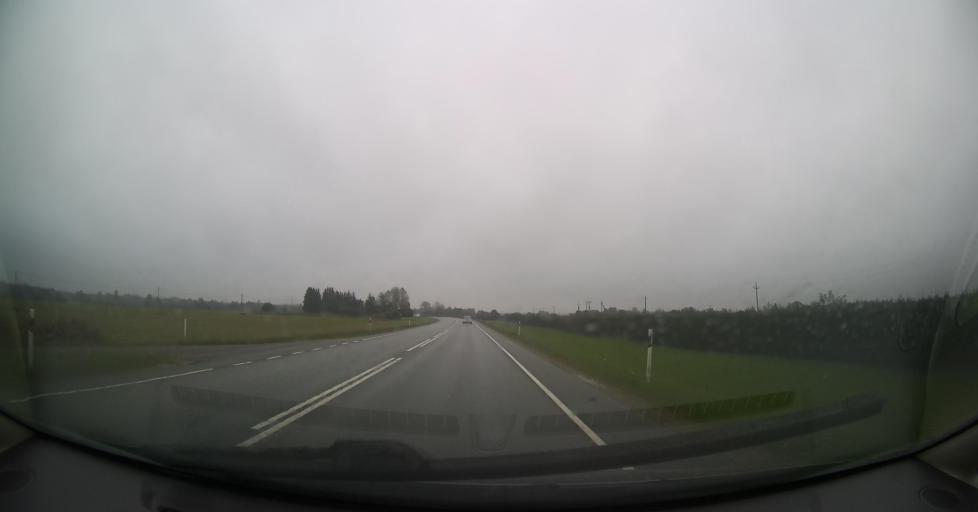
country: EE
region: Jaervamaa
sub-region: Paide linn
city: Paide
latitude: 58.8905
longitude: 25.6687
